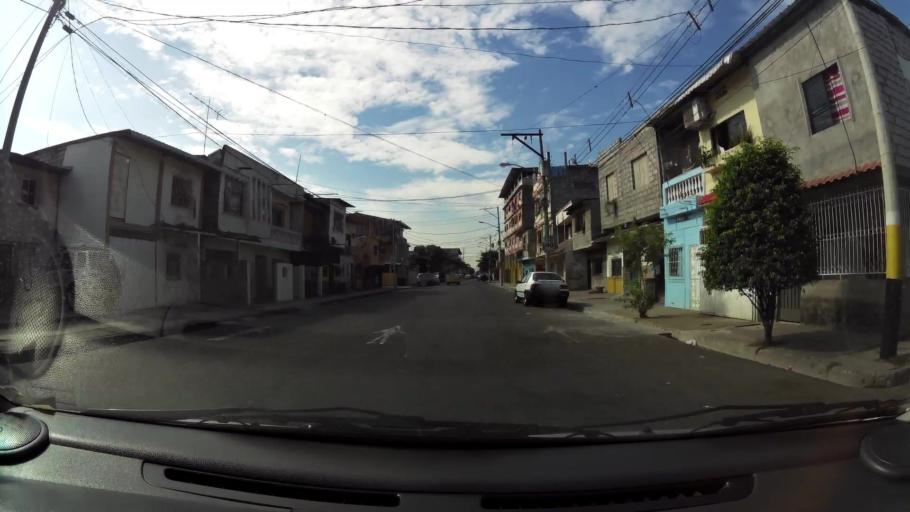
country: EC
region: Guayas
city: Guayaquil
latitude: -2.2182
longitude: -79.9053
